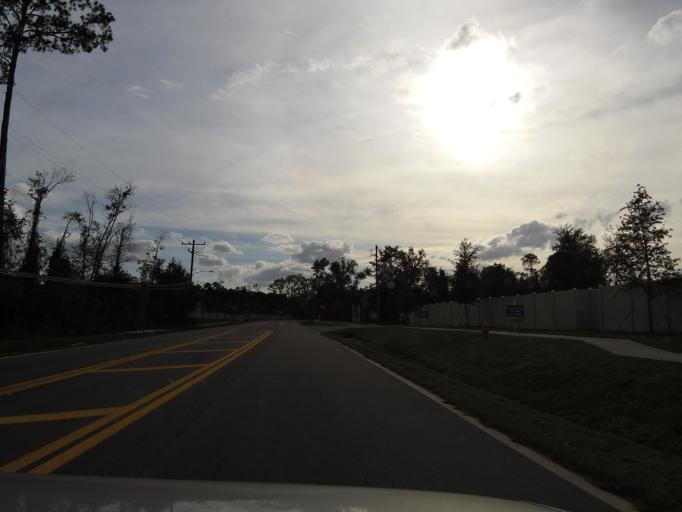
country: US
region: Florida
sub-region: Duval County
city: Jacksonville
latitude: 30.4525
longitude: -81.6849
